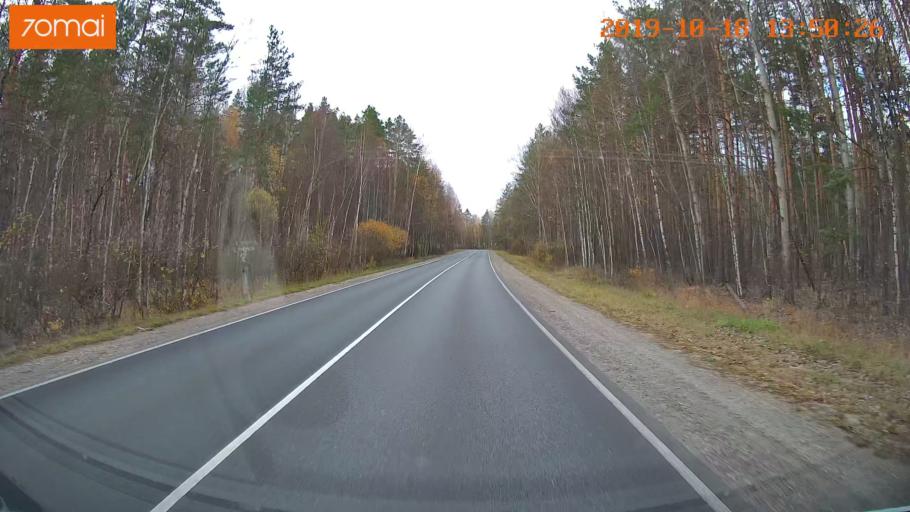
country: RU
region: Moskovskaya
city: Radovitskiy
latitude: 55.0062
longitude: 39.9711
